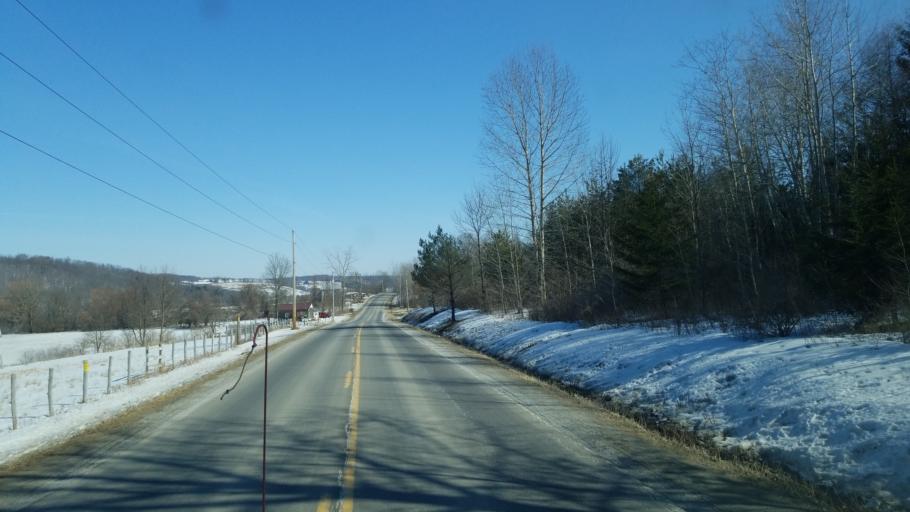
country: US
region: Pennsylvania
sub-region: Tioga County
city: Elkland
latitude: 42.0587
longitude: -77.4464
